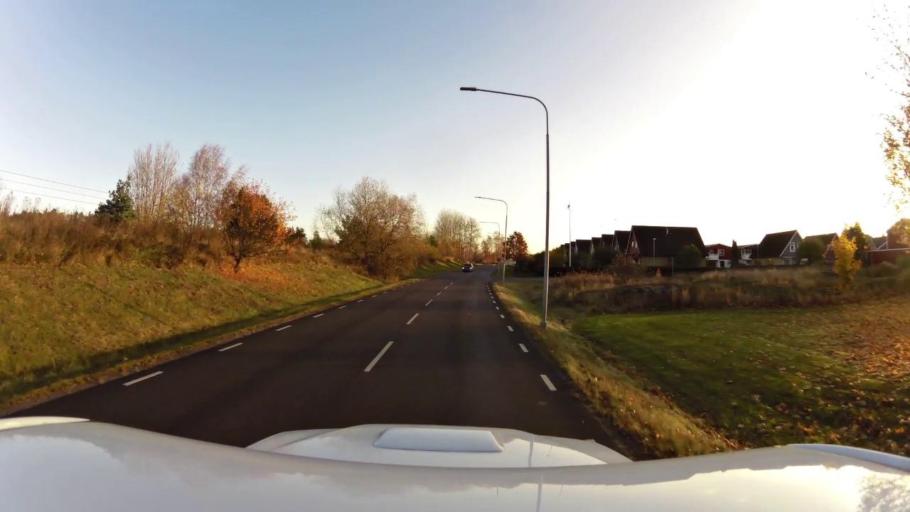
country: SE
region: OEstergoetland
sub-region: Linkopings Kommun
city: Ekangen
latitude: 58.4326
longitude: 15.6803
